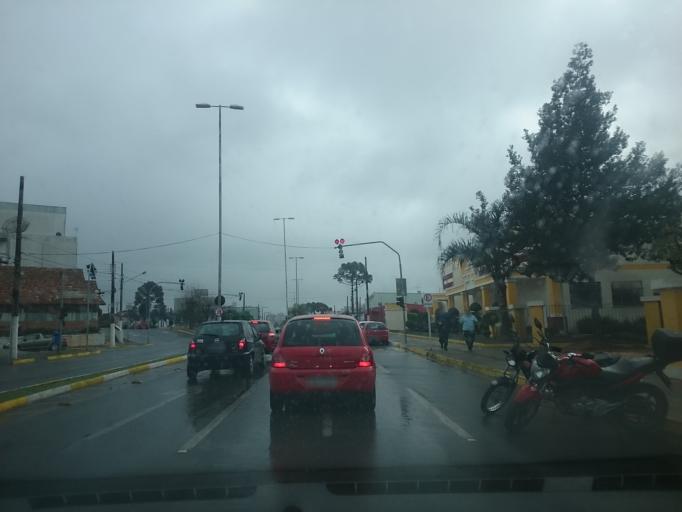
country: BR
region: Santa Catarina
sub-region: Lages
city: Lages
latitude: -27.8244
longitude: -50.3342
